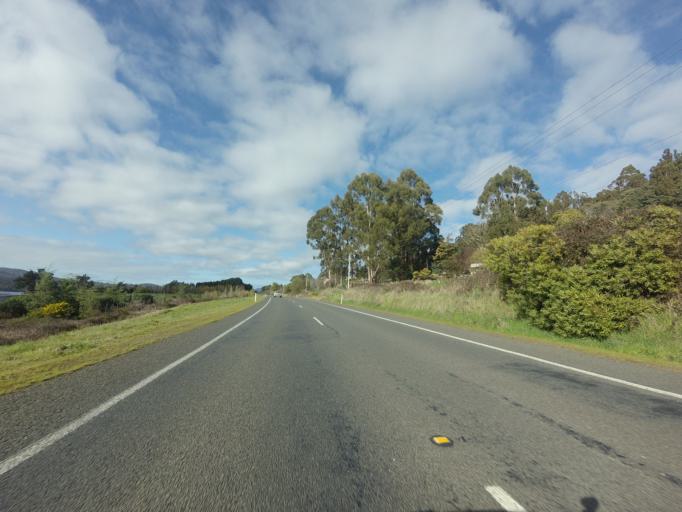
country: AU
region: Tasmania
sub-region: Huon Valley
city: Franklin
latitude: -43.1198
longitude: 146.9905
